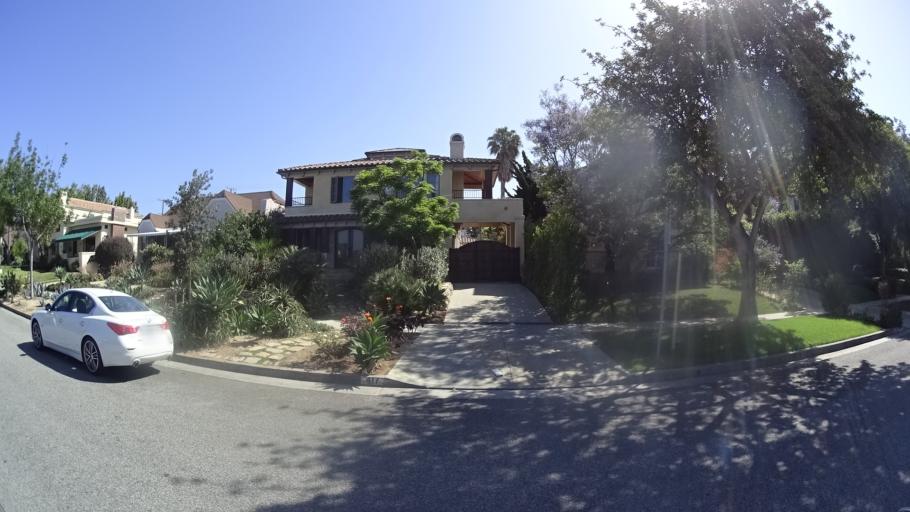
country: US
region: California
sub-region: Los Angeles County
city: Santa Monica
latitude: 34.0345
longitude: -118.5016
